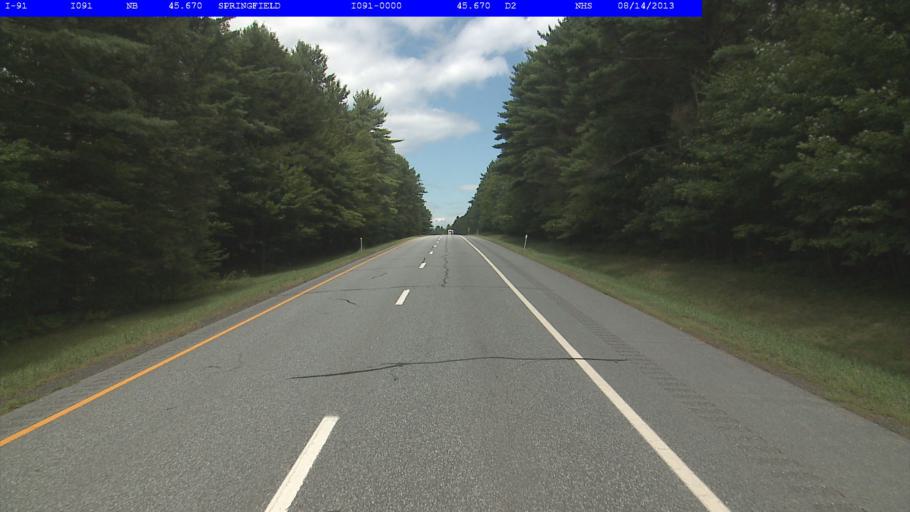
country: US
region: Vermont
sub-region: Windsor County
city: Springfield
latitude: 43.3222
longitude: -72.4197
